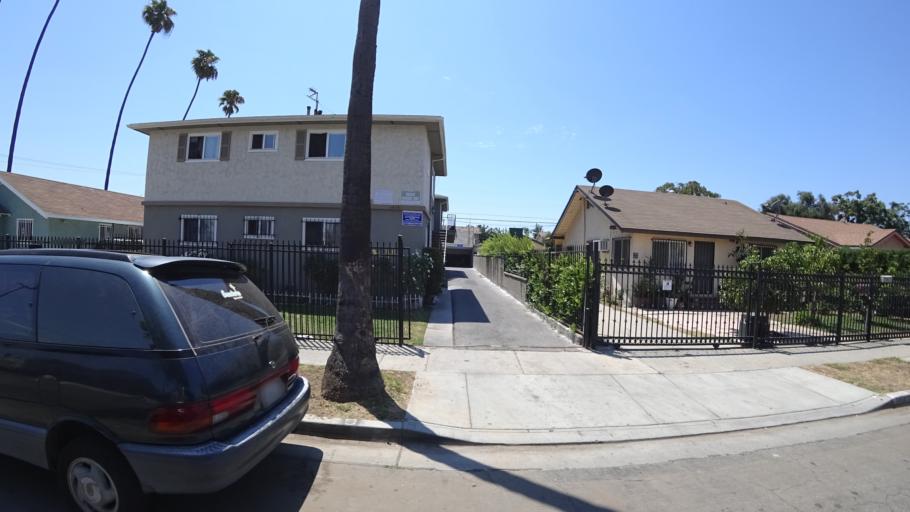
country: US
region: California
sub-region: Los Angeles County
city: Westmont
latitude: 33.9532
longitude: -118.2963
